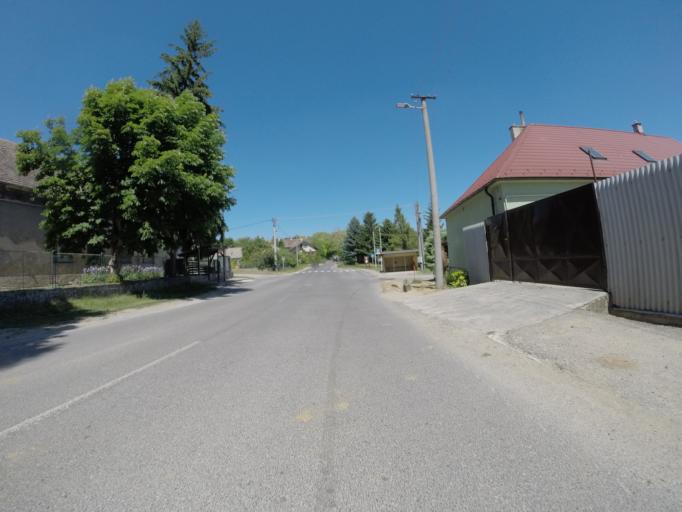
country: SK
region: Trnavsky
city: Hlohovec
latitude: 48.4657
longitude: 17.8525
